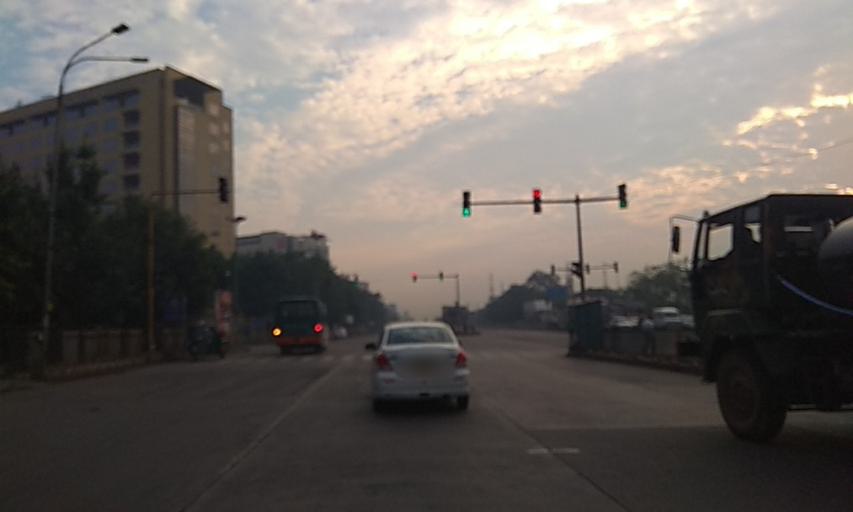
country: IN
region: Maharashtra
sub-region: Pune Division
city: Lohogaon
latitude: 18.5586
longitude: 73.9110
